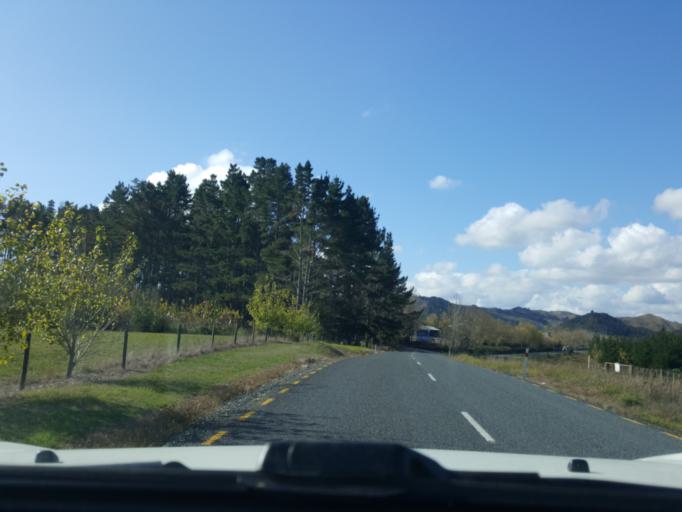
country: NZ
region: Waikato
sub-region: Waikato District
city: Te Kauwhata
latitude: -37.5324
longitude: 175.1804
